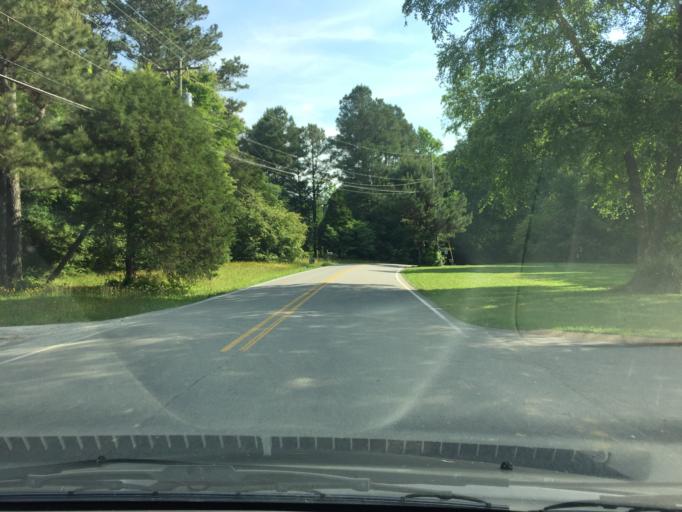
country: US
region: Tennessee
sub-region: Hamilton County
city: Collegedale
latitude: 35.0684
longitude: -85.0086
